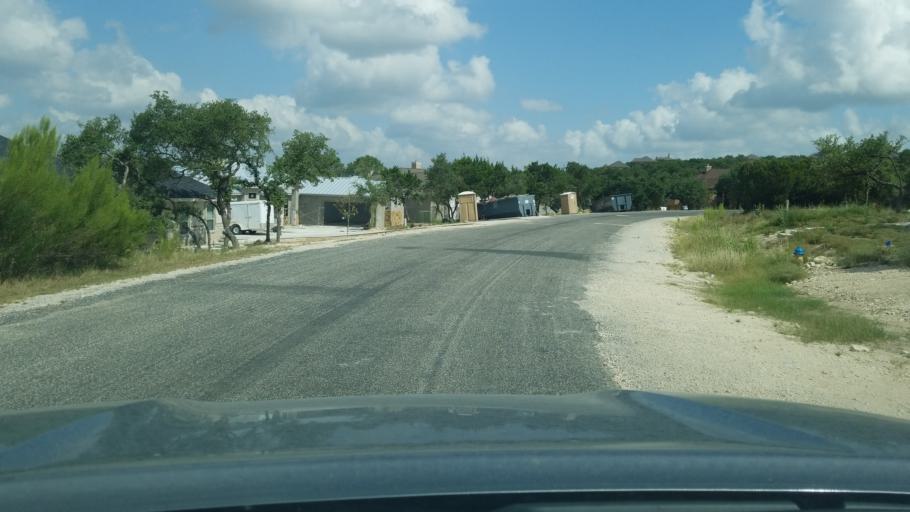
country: US
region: Texas
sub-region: Bexar County
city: Timberwood Park
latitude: 29.6848
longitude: -98.5207
